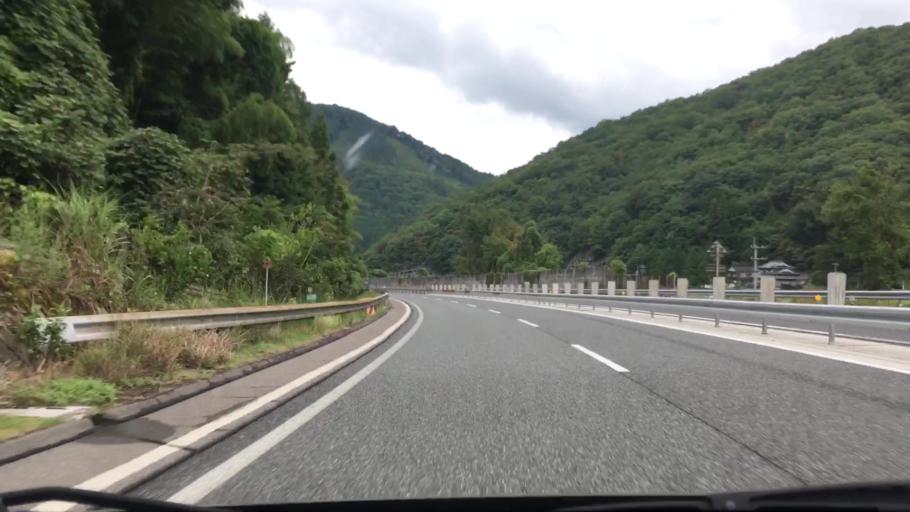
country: JP
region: Okayama
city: Niimi
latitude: 35.0109
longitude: 133.4934
